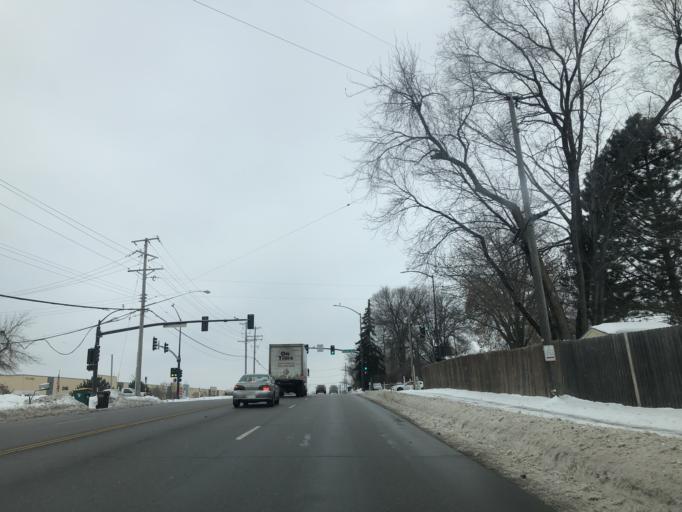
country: US
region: Minnesota
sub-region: Hennepin County
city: Osseo
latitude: 45.0946
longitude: -93.3911
